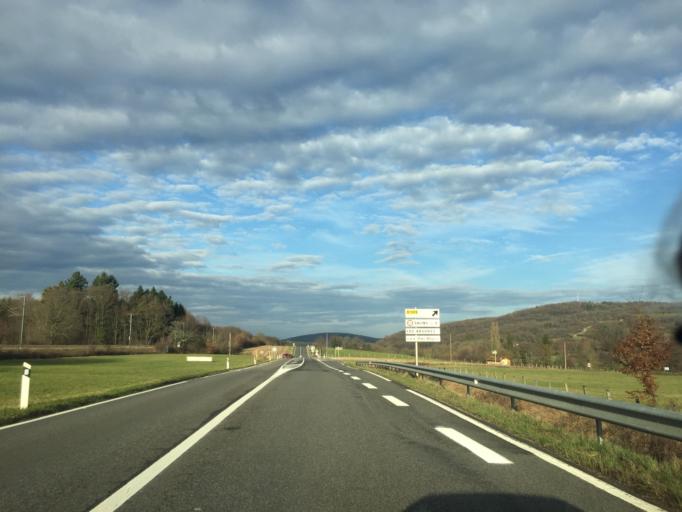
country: FR
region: Franche-Comte
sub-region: Departement du Jura
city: Mouchard
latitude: 46.9441
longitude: 5.7803
